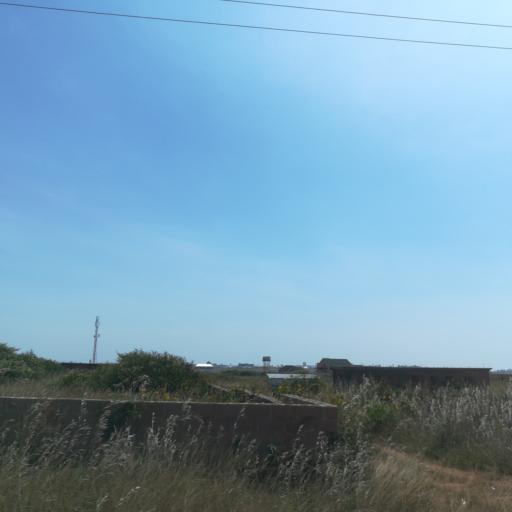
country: NG
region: Plateau
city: Bukuru
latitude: 9.8469
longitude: 8.9186
